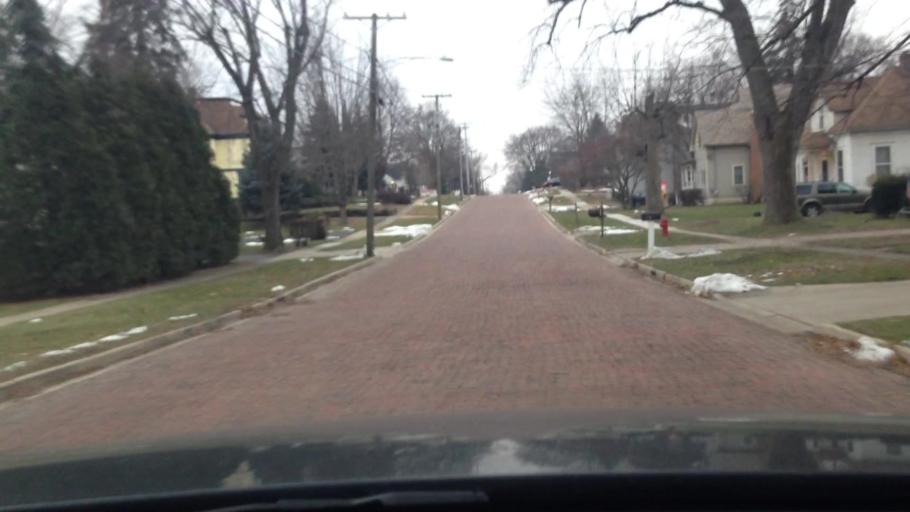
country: US
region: Illinois
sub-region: McHenry County
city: Huntley
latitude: 42.1731
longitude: -88.4264
